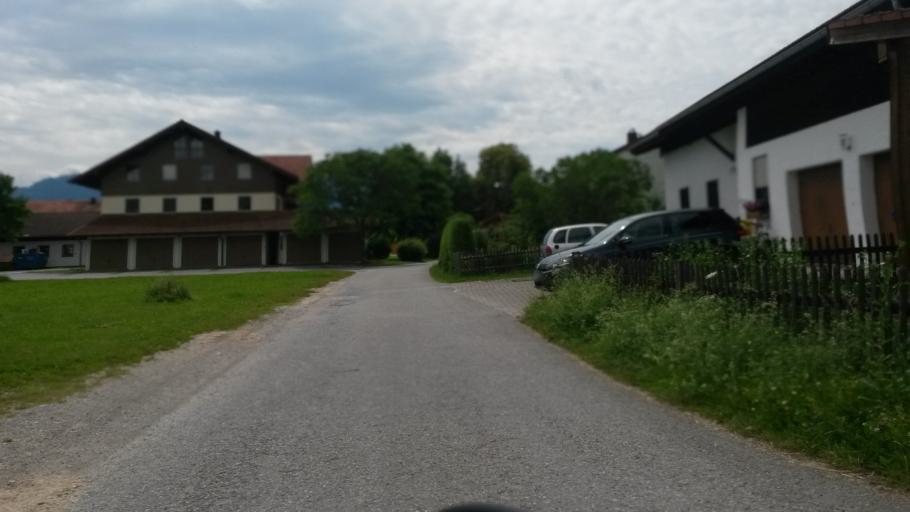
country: DE
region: Bavaria
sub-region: Upper Bavaria
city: Ubersee
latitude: 47.8444
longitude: 12.4894
